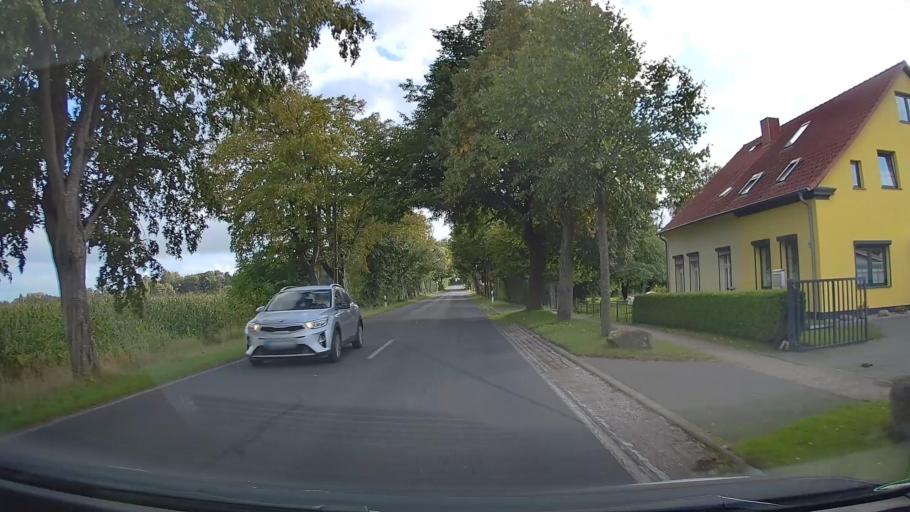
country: DE
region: Mecklenburg-Vorpommern
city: Putbus
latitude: 54.3611
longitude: 13.4770
